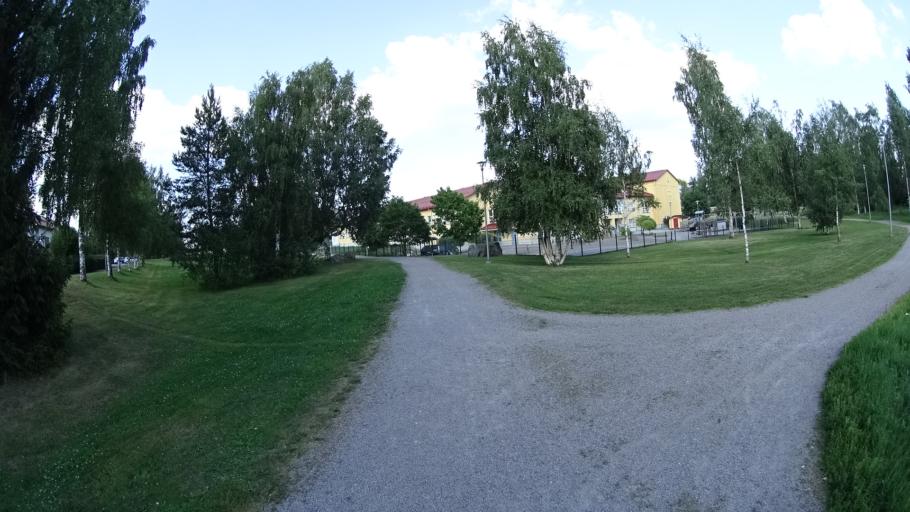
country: FI
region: Uusimaa
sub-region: Porvoo
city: Porvoo
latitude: 60.4080
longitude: 25.6621
